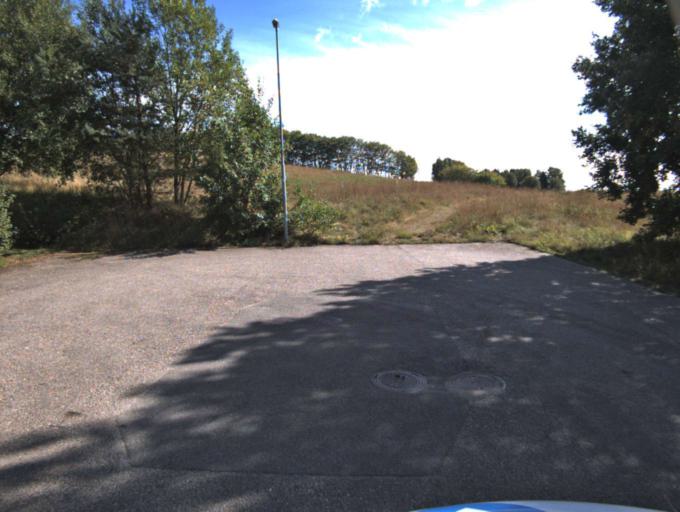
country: SE
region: Vaestra Goetaland
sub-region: Ulricehamns Kommun
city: Ulricehamn
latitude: 57.8190
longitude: 13.5338
